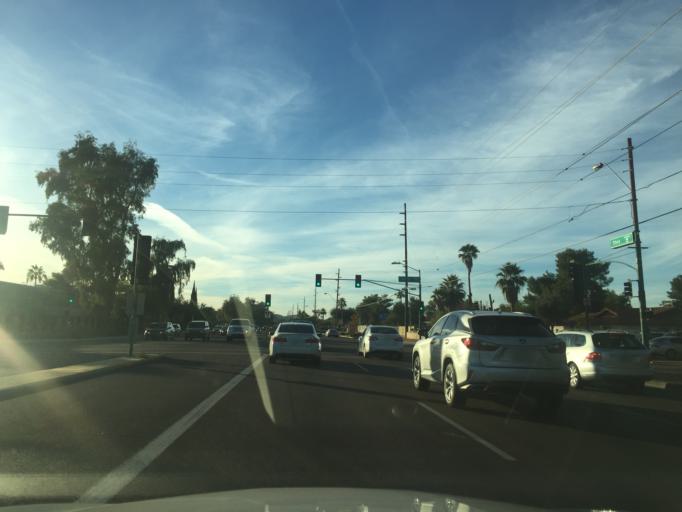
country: US
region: Arizona
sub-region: Maricopa County
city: Paradise Valley
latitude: 33.5827
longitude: -111.9601
